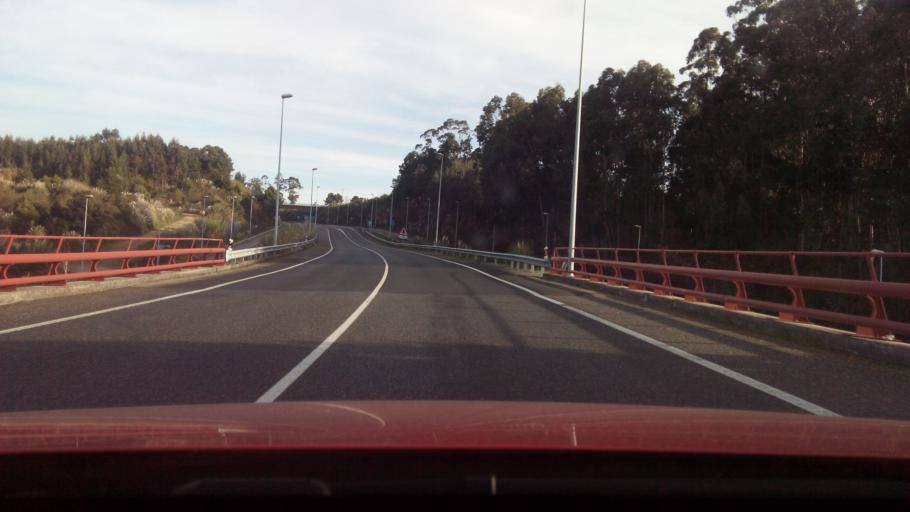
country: ES
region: Galicia
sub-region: Provincia de Pontevedra
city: Sanxenxo
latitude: 42.4151
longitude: -8.8120
